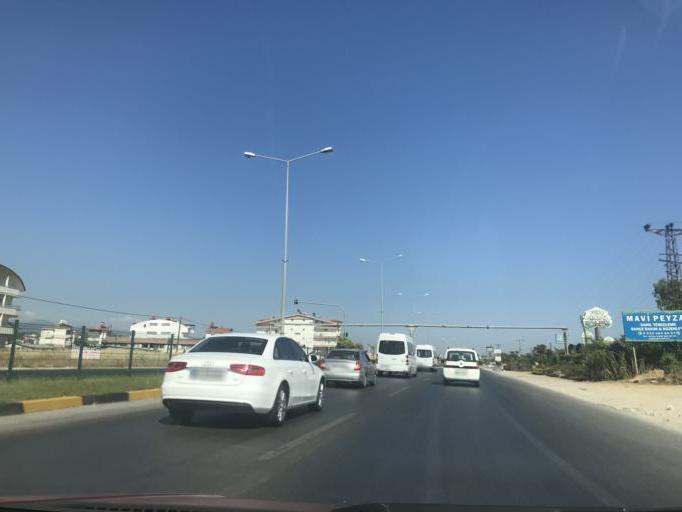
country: TR
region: Antalya
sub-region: Manavgat
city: Side
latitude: 36.8149
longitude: 31.3668
